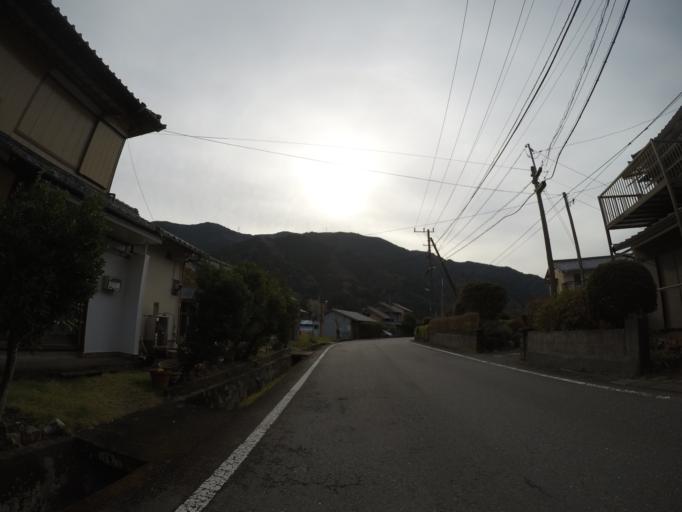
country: JP
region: Shizuoka
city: Heda
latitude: 34.8495
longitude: 138.7946
